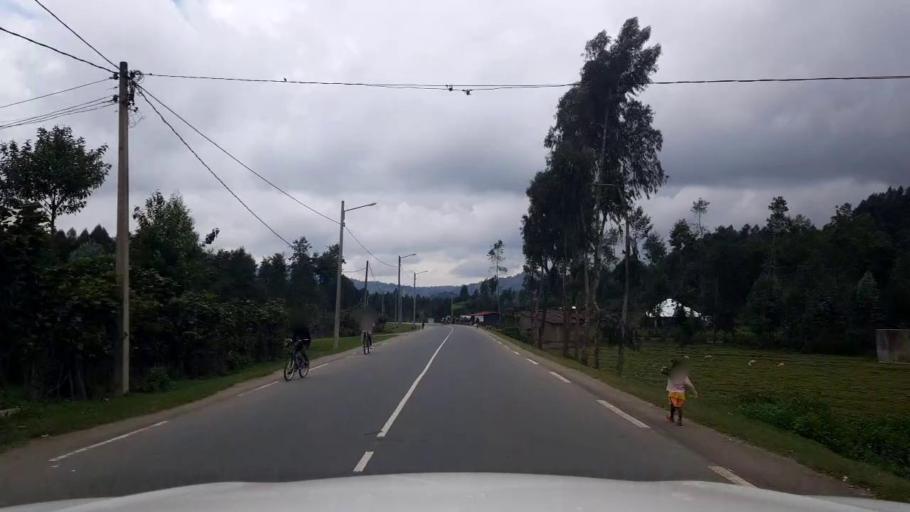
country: RW
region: Northern Province
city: Musanze
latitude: -1.6183
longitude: 29.5037
